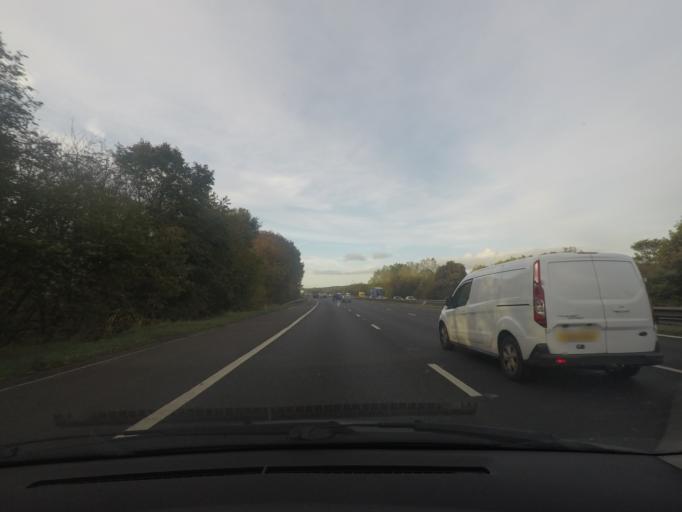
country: GB
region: England
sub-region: Barnsley
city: Darton
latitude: 53.5878
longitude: -1.5363
